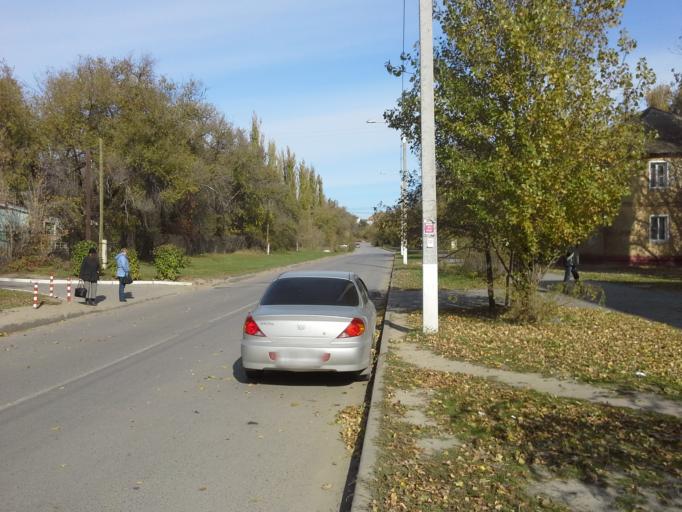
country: RU
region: Volgograd
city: Vodstroy
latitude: 48.8403
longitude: 44.6380
